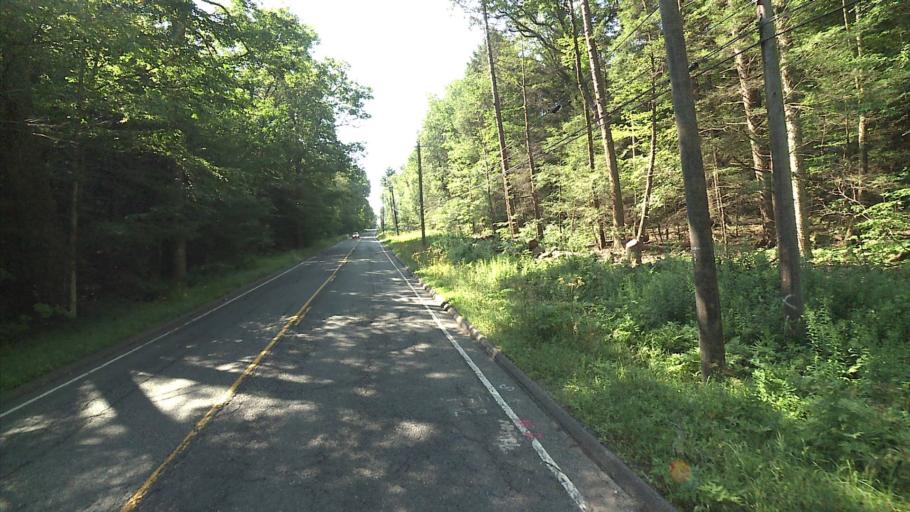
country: US
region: Connecticut
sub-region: Litchfield County
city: Winsted
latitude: 42.0118
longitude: -73.1108
